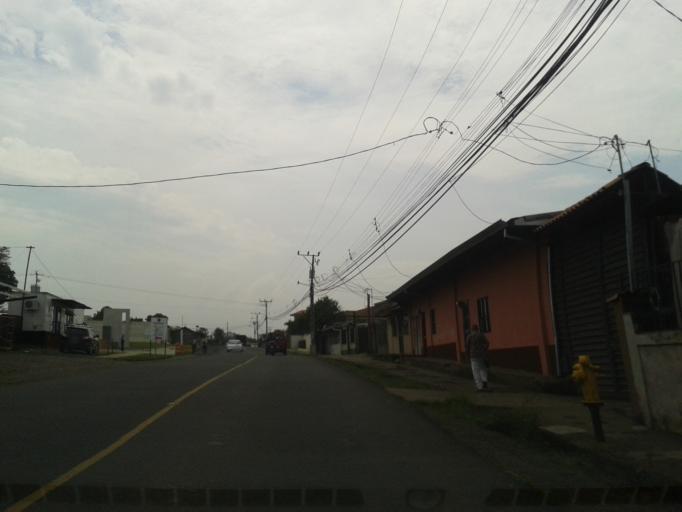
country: CR
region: Heredia
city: San Pablo
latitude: 9.9798
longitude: -84.0978
